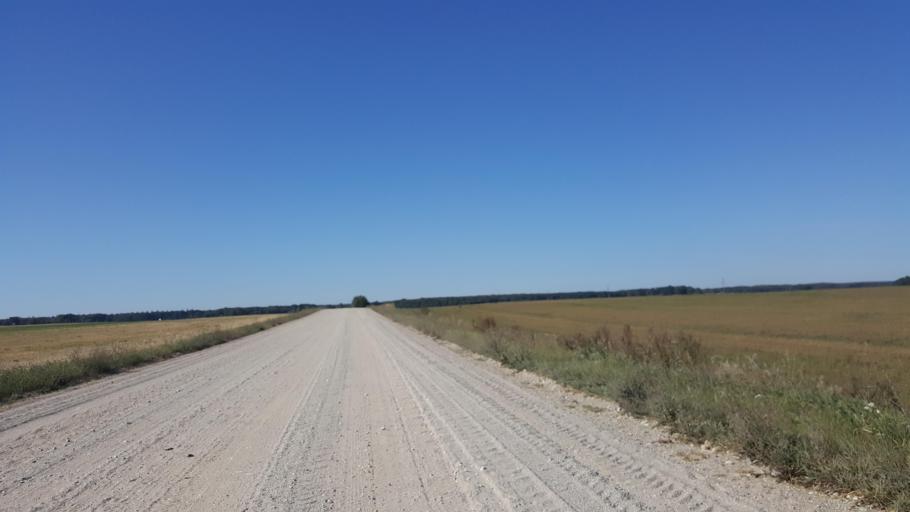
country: BY
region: Brest
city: Charnawchytsy
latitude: 52.3353
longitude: 23.6312
